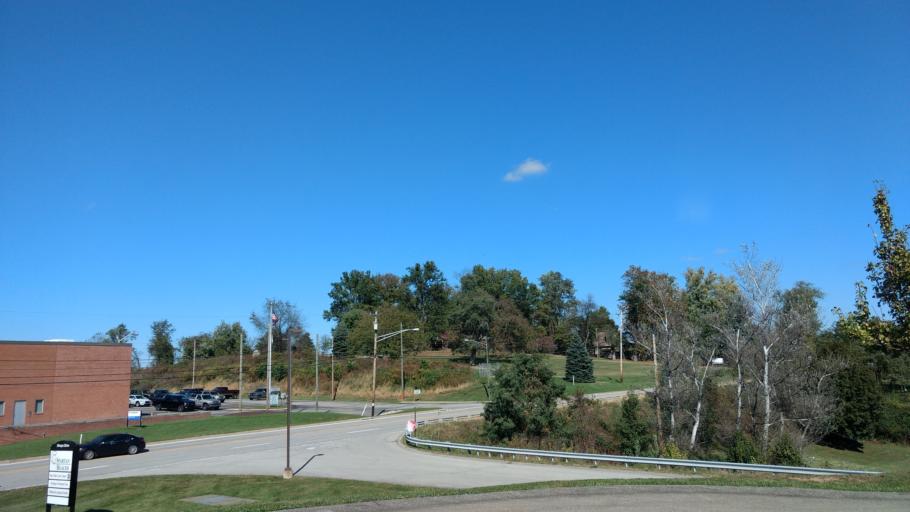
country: US
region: Pennsylvania
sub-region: Washington County
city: North Charleroi
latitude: 40.1628
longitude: -79.9240
